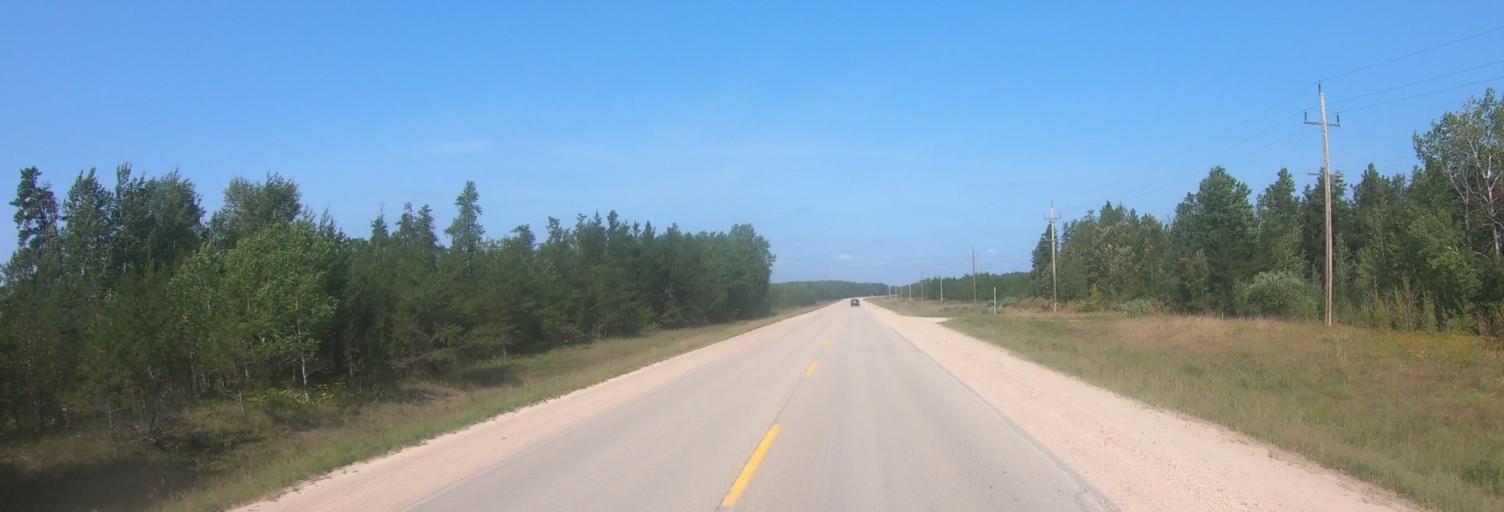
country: US
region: Minnesota
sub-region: Roseau County
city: Roseau
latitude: 49.1368
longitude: -96.0960
